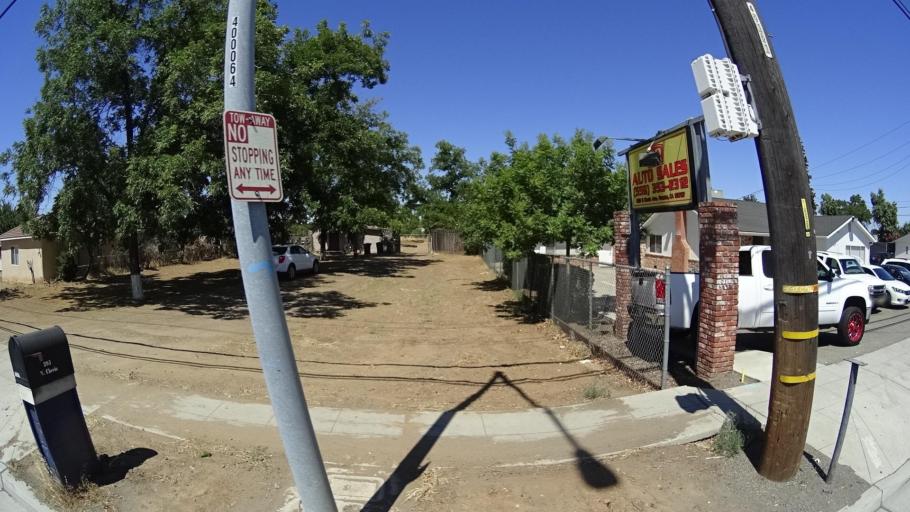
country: US
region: California
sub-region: Fresno County
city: Sunnyside
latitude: 36.7469
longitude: -119.7002
